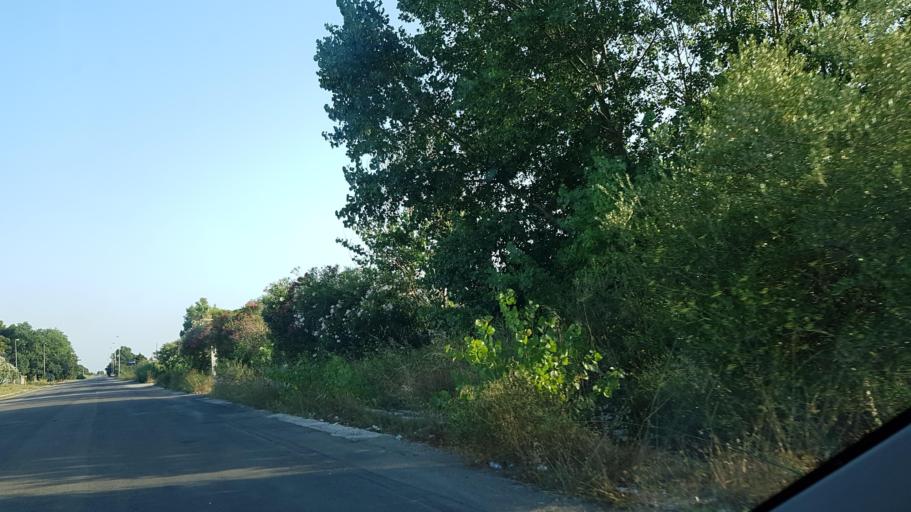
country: IT
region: Apulia
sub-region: Provincia di Brindisi
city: Materdomini
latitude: 40.6333
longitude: 17.9735
